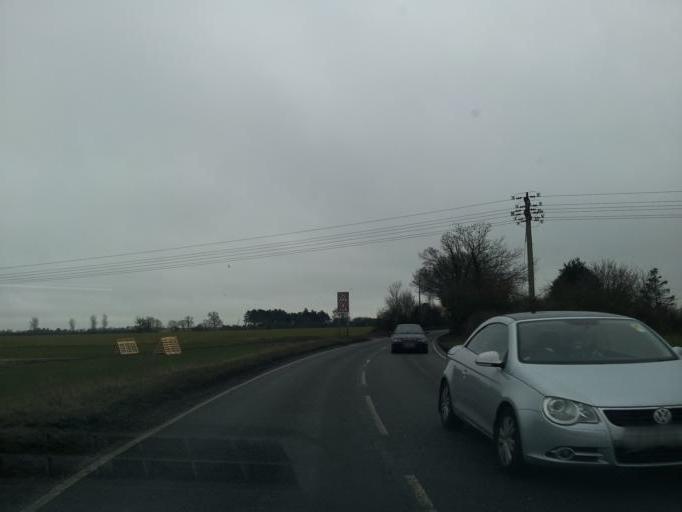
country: GB
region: England
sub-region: Essex
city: Mistley
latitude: 51.9173
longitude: 1.0865
